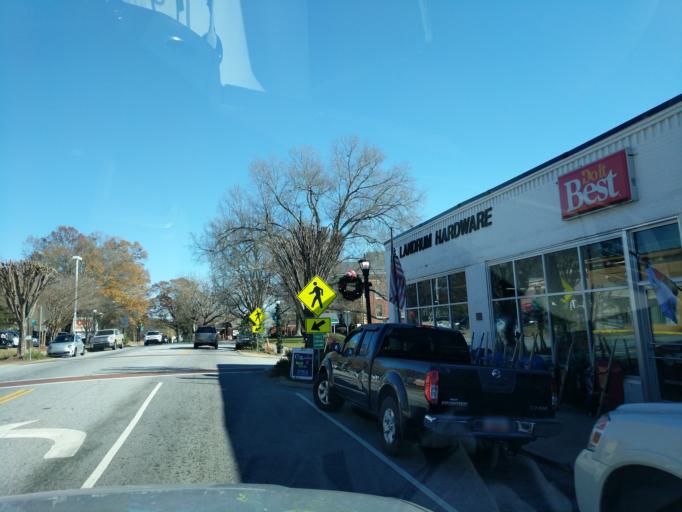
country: US
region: South Carolina
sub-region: Spartanburg County
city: Landrum
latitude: 35.1753
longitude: -82.1878
